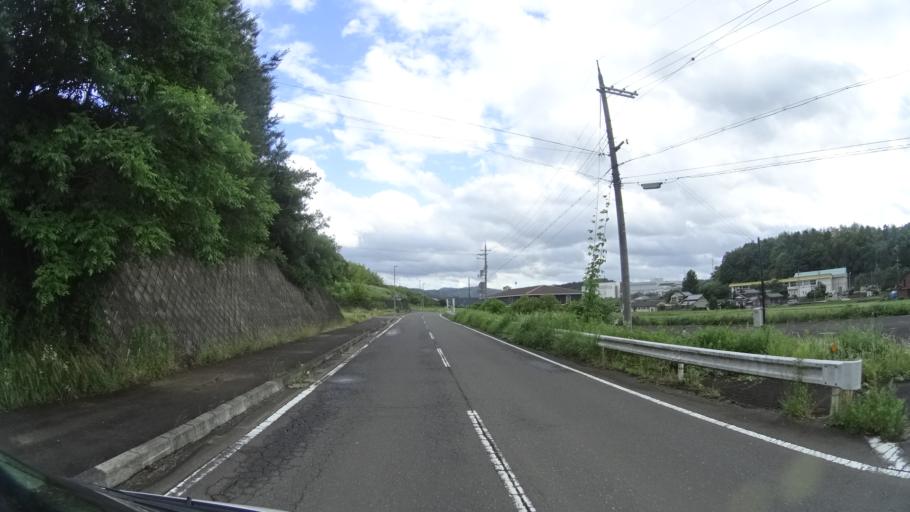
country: JP
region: Kyoto
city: Ayabe
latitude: 35.3370
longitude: 135.2938
